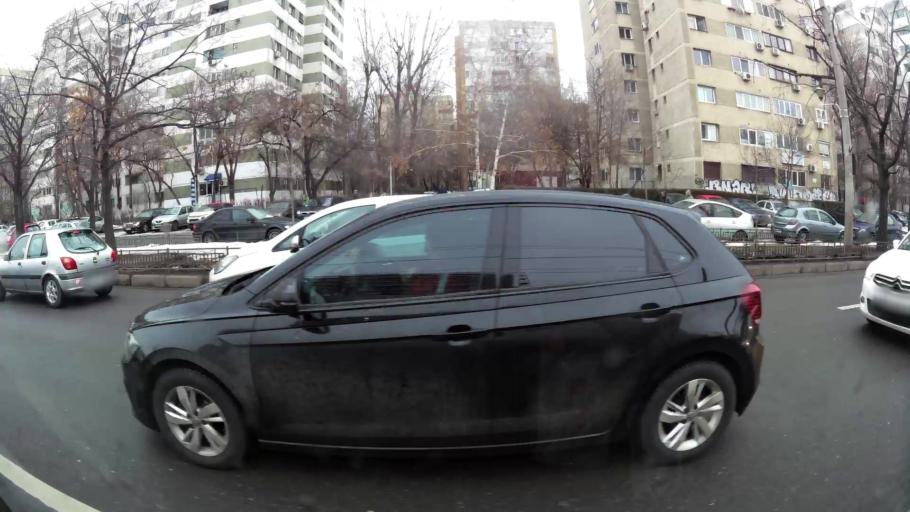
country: RO
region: Ilfov
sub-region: Comuna Chiajna
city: Rosu
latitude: 44.4261
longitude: 26.0336
